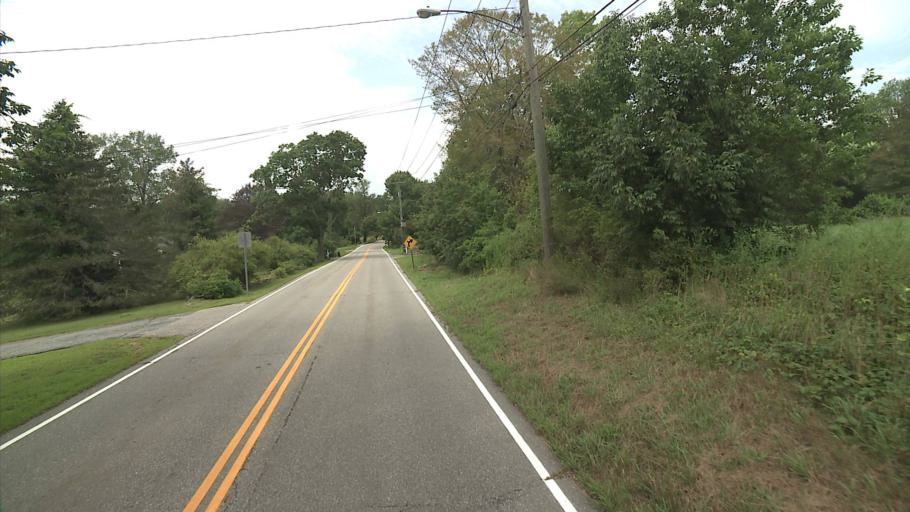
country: US
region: Connecticut
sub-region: Windham County
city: Wauregan
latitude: 41.7800
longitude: -71.9472
